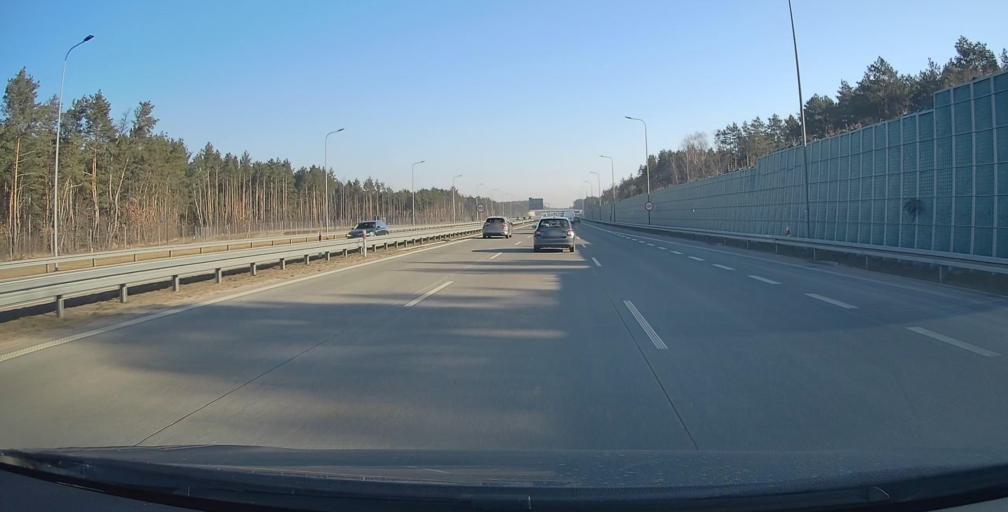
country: PL
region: Masovian Voivodeship
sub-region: Powiat otwocki
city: Jozefow
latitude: 52.1747
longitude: 21.2159
